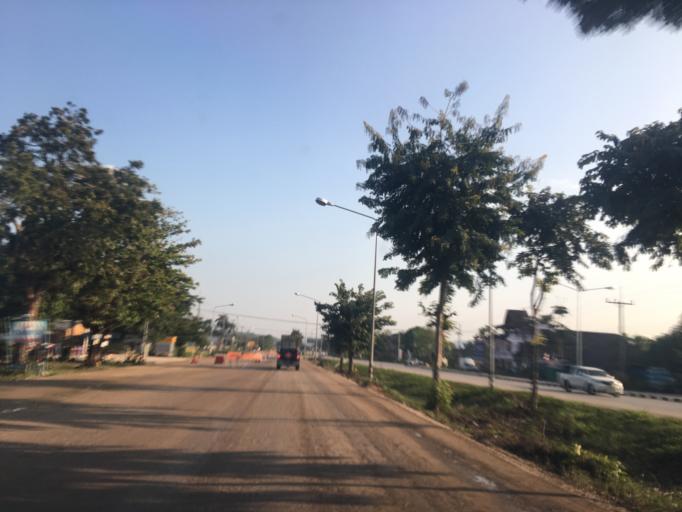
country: TH
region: Lampang
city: Ngao
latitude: 18.7475
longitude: 99.9728
